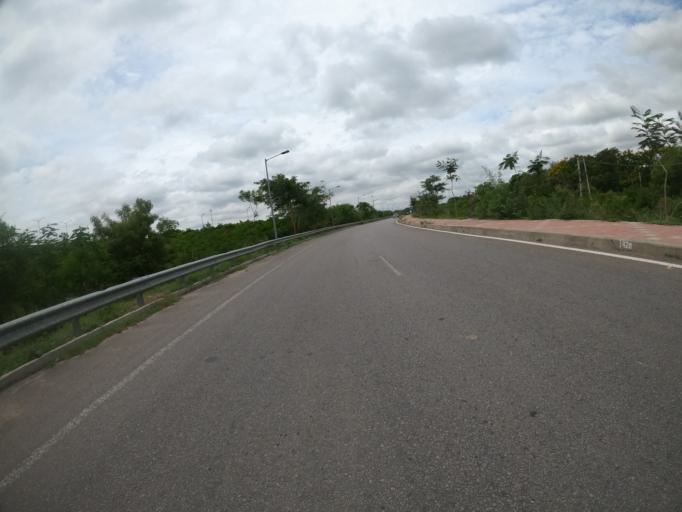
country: IN
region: Telangana
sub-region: Rangareddi
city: Sriramnagar
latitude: 17.2532
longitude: 78.3760
